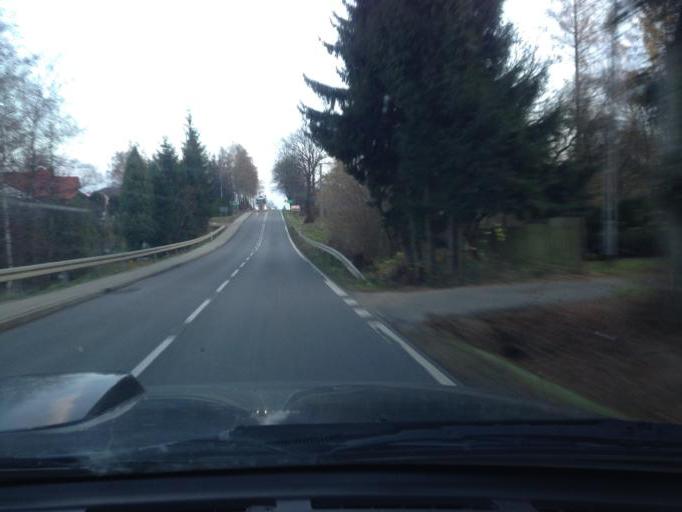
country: PL
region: Subcarpathian Voivodeship
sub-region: Powiat jasielski
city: Osiek Jasielski
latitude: 49.6406
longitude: 21.5199
